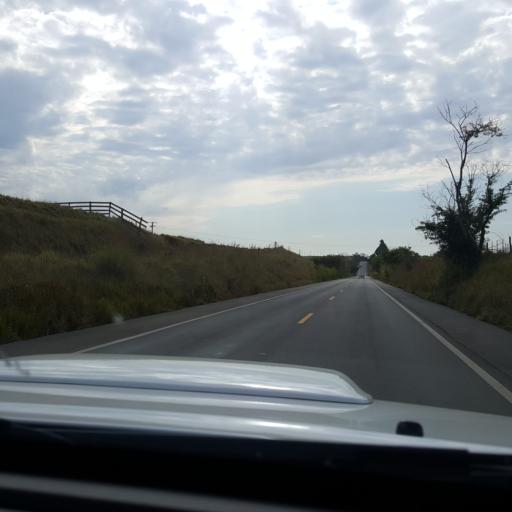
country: BR
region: Sao Paulo
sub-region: Itaporanga
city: Itaporanga
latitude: -23.7580
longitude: -49.4501
